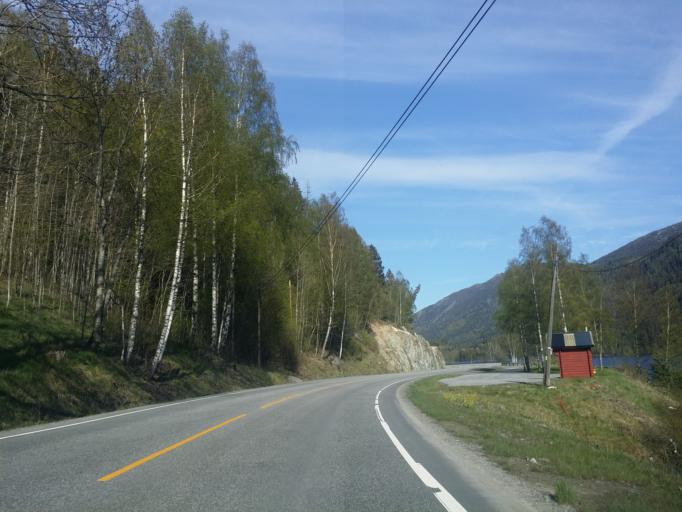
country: NO
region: Telemark
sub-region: Seljord
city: Seljord
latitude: 59.6054
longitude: 8.7194
